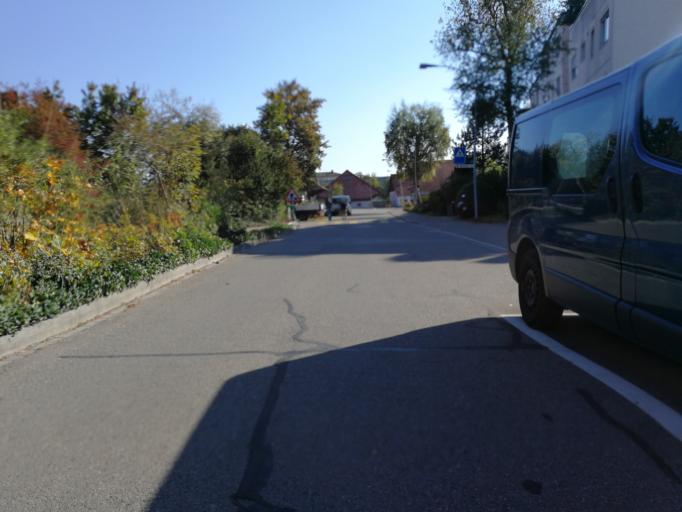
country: CH
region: Zurich
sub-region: Bezirk Uster
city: Monchaltorf
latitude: 47.3115
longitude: 8.7189
